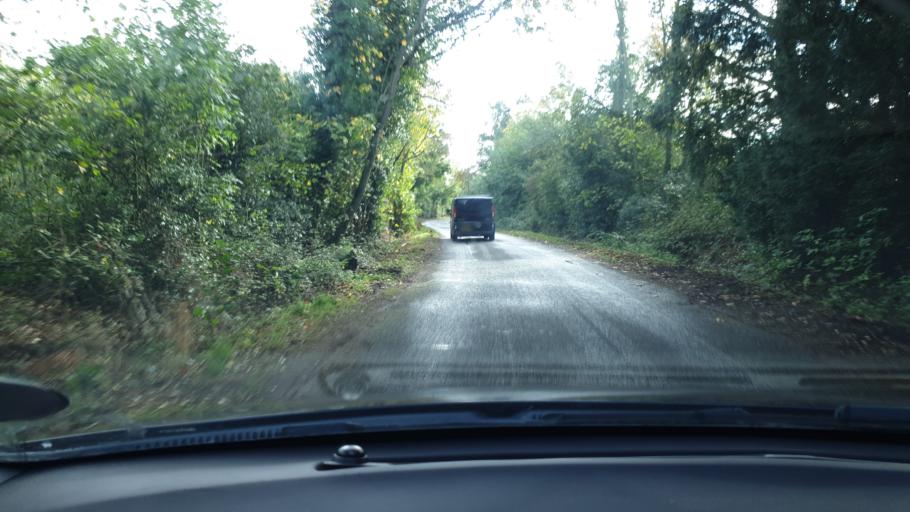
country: GB
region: England
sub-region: Essex
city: Alresford
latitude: 51.8586
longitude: 1.0264
